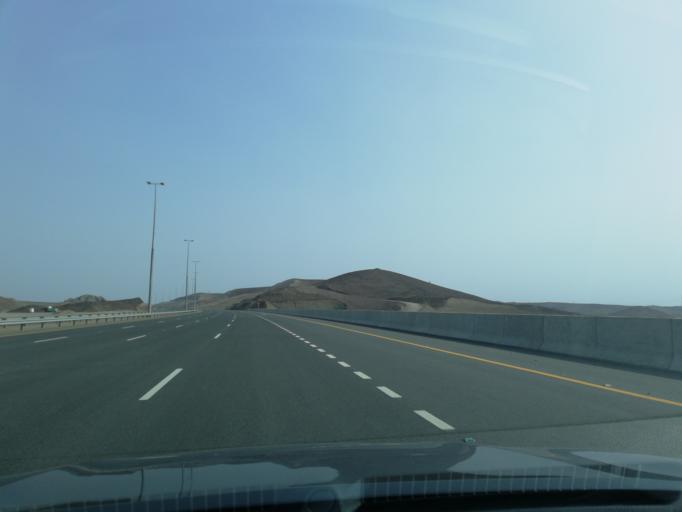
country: OM
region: Al Batinah
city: Al Liwa'
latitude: 24.3570
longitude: 56.5500
